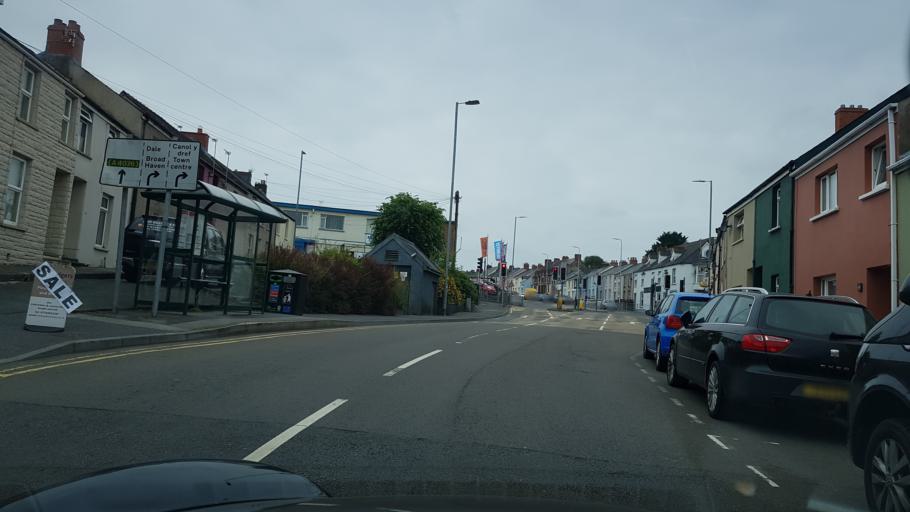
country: GB
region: Wales
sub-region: Pembrokeshire
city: Haverfordwest
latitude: 51.7985
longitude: -4.9740
